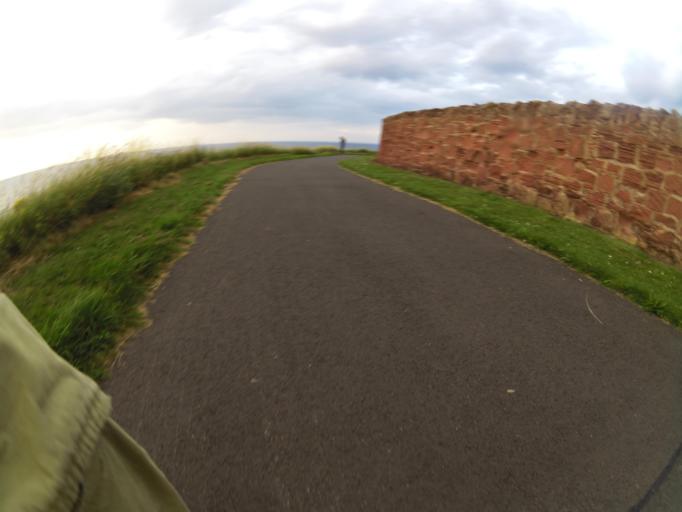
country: GB
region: Scotland
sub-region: East Lothian
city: Dunbar
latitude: 56.0064
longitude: -2.5318
